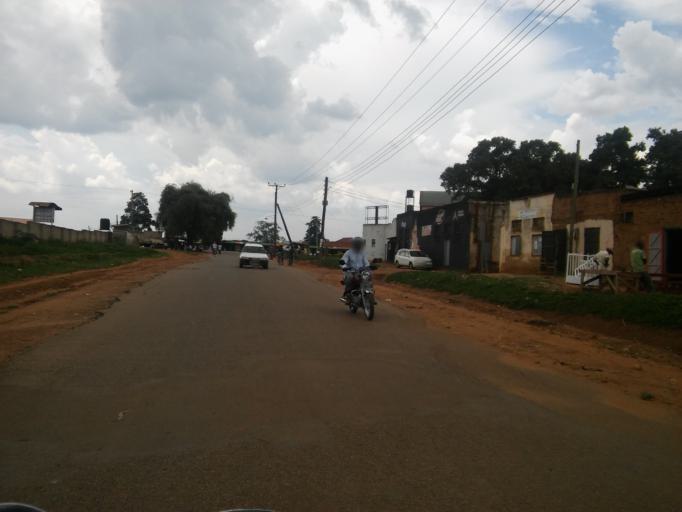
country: UG
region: Eastern Region
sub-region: Mbale District
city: Mbale
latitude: 1.0784
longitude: 34.1609
